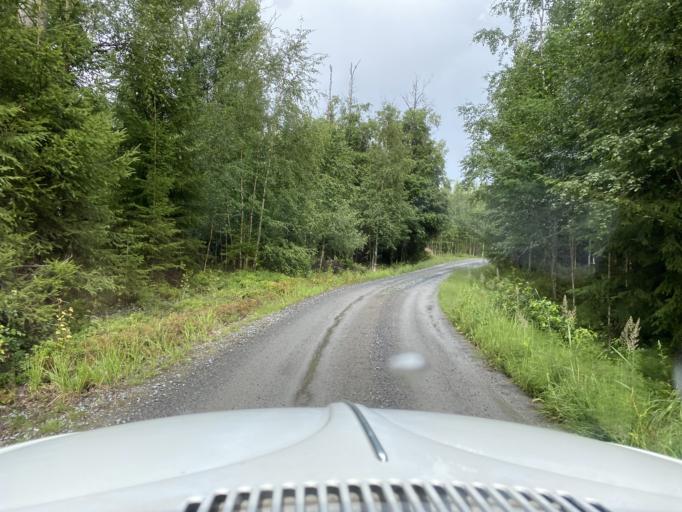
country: FI
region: Pirkanmaa
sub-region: Lounais-Pirkanmaa
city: Punkalaidun
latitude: 61.1351
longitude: 23.0682
